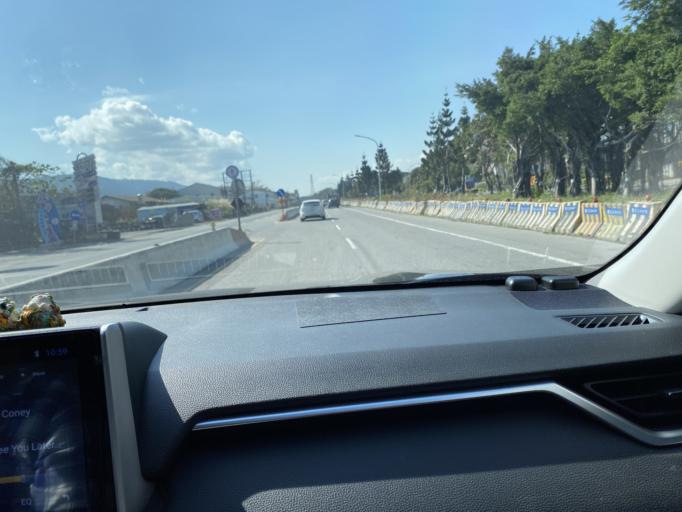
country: TW
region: Taiwan
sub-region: Hualien
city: Hualian
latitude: 23.9307
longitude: 121.5942
